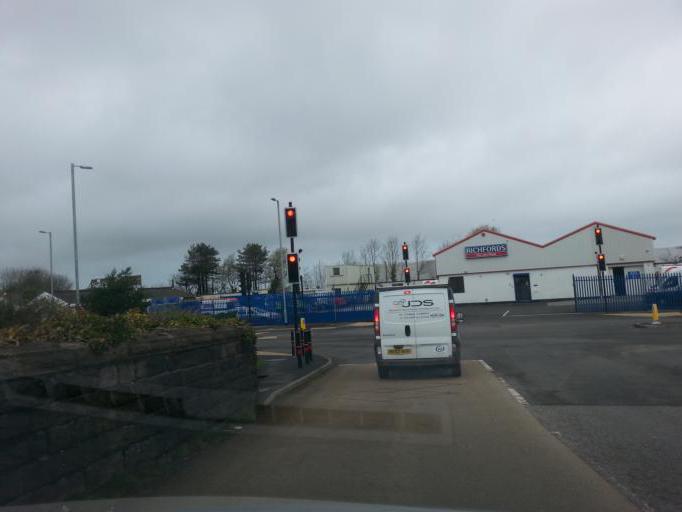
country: GB
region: England
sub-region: Cornwall
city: Camborne
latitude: 50.2209
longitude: -5.2690
